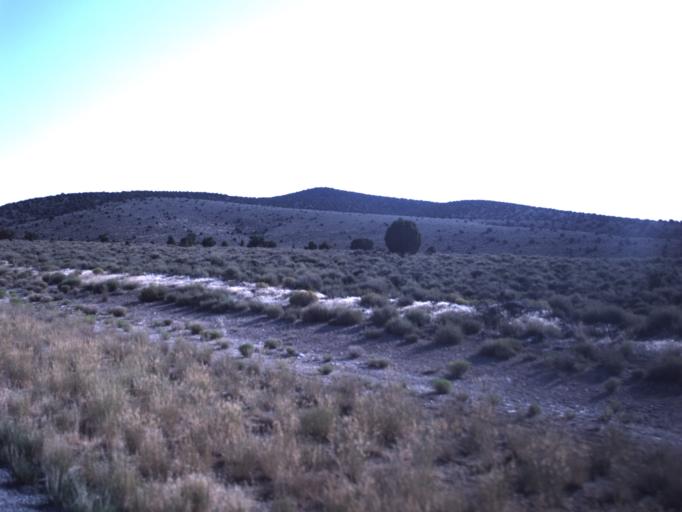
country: US
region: Utah
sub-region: Iron County
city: Parowan
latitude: 38.0219
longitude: -112.9981
